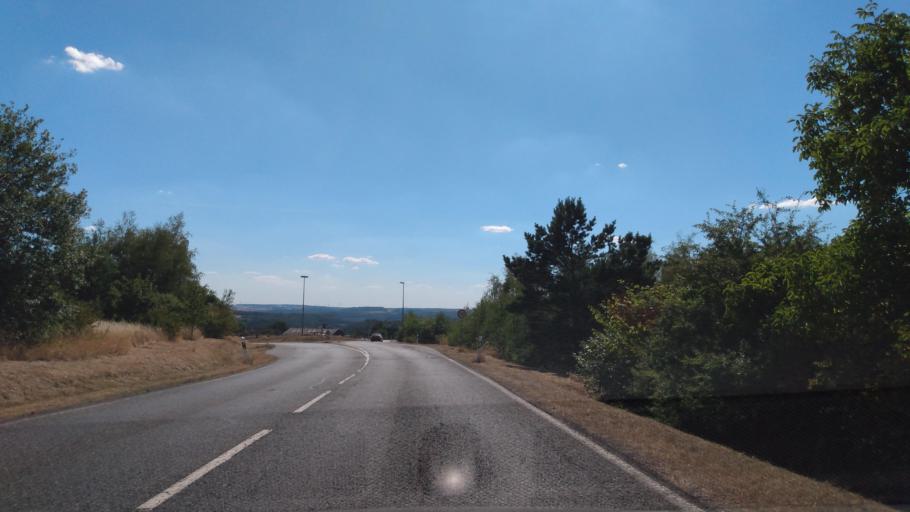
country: DE
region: Rheinland-Pfalz
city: Spangdahlem
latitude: 49.9821
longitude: 6.6881
